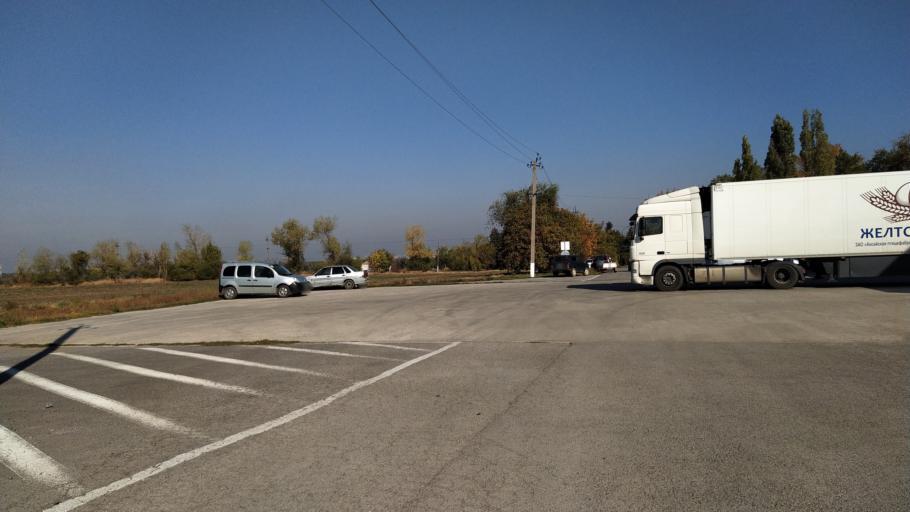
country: RU
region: Rostov
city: Bataysk
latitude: 47.0878
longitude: 39.7772
